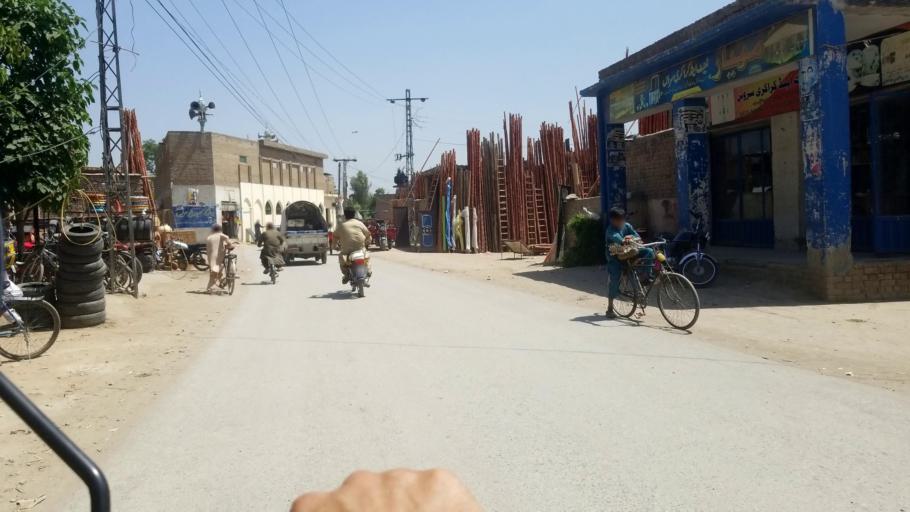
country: PK
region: Khyber Pakhtunkhwa
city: Peshawar
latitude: 34.0300
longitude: 71.4863
